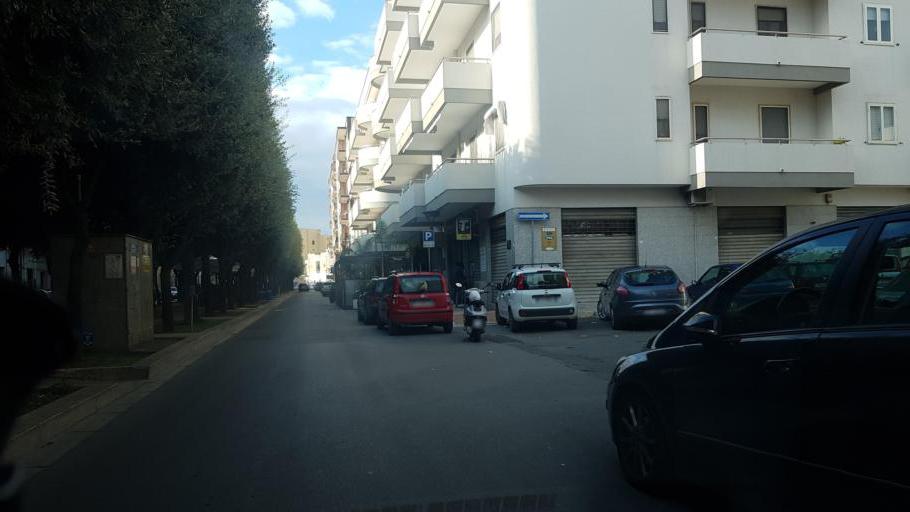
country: IT
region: Apulia
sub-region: Provincia di Brindisi
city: Francavilla Fontana
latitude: 40.5271
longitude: 17.5881
